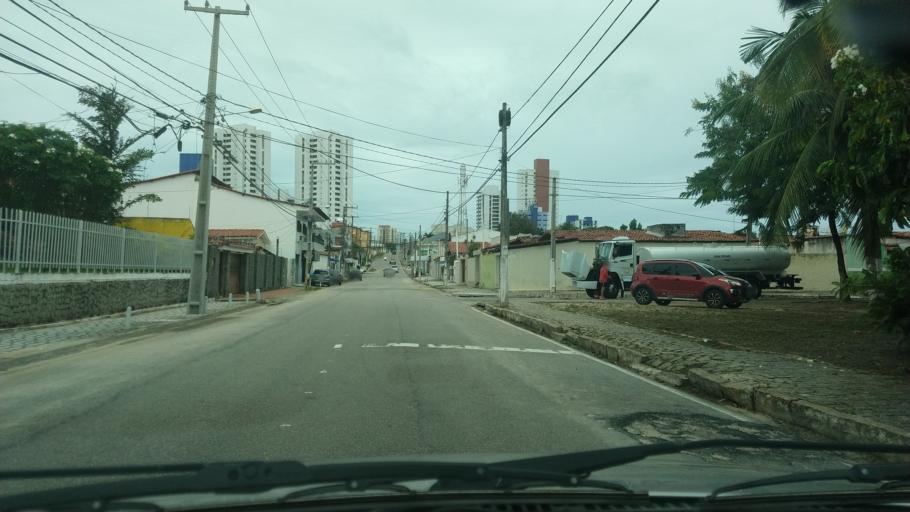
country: BR
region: Rio Grande do Norte
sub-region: Natal
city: Natal
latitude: -5.8549
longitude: -35.2078
